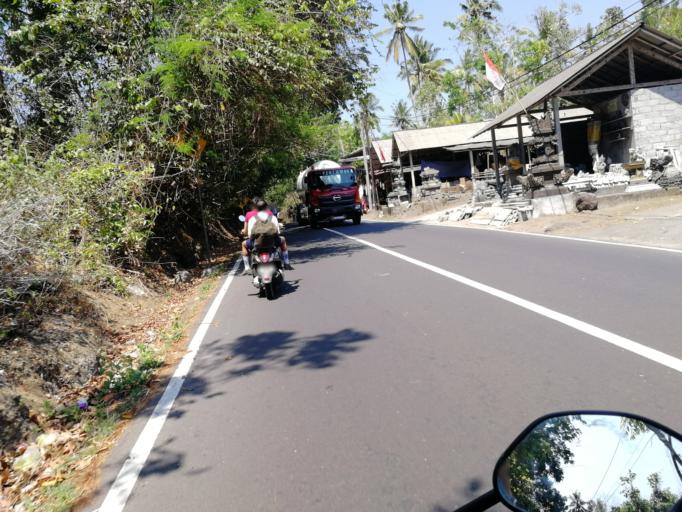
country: ID
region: Bali
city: Abang
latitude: -8.3908
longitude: 115.5978
